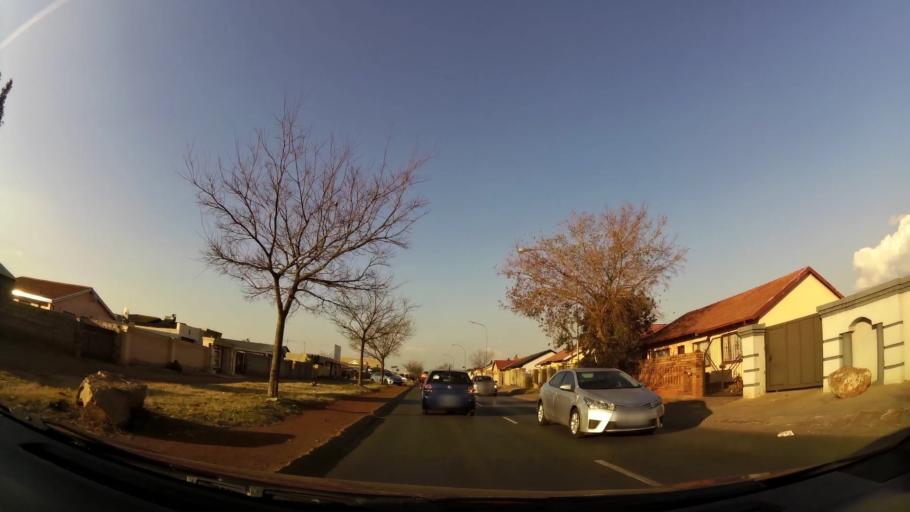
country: ZA
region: Gauteng
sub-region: City of Johannesburg Metropolitan Municipality
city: Soweto
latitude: -26.2292
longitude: 27.8492
